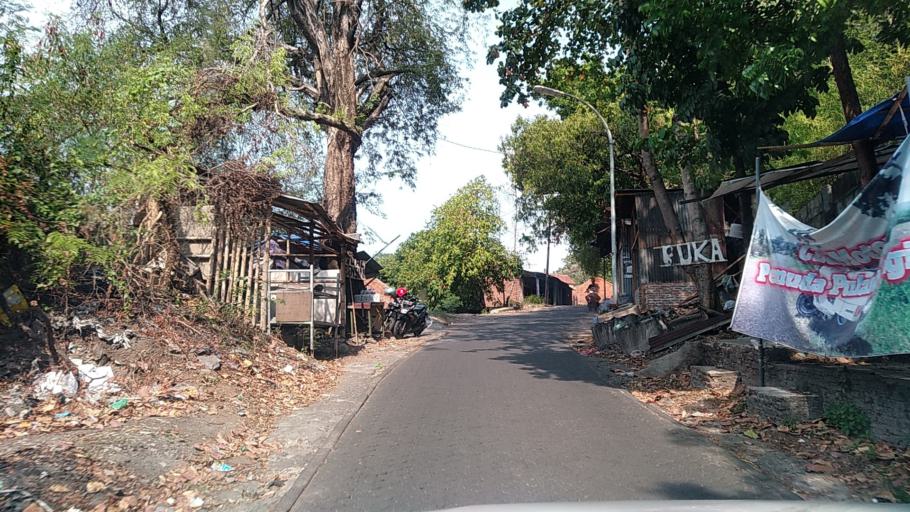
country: ID
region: Central Java
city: Semarang
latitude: -6.9912
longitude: 110.4079
